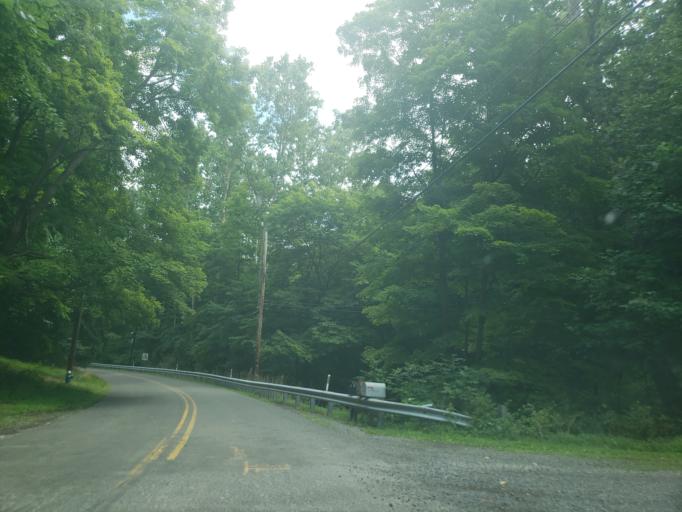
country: US
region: Pennsylvania
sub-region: Allegheny County
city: Coraopolis
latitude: 40.5354
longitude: -80.1310
